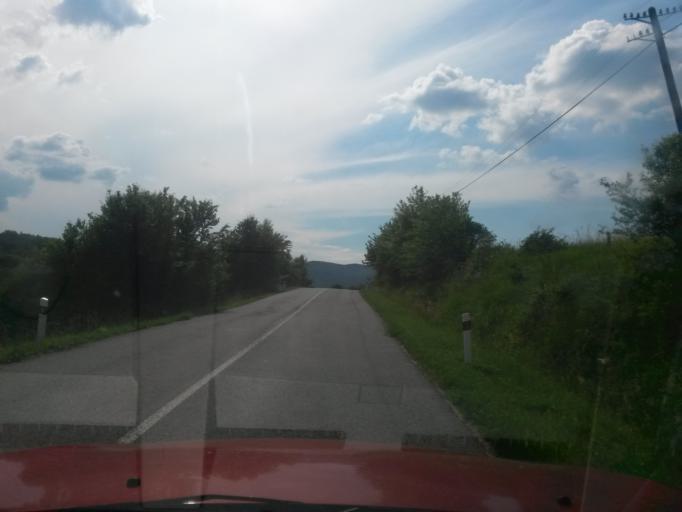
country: SK
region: Presovsky
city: Snina
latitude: 49.1273
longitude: 22.1109
